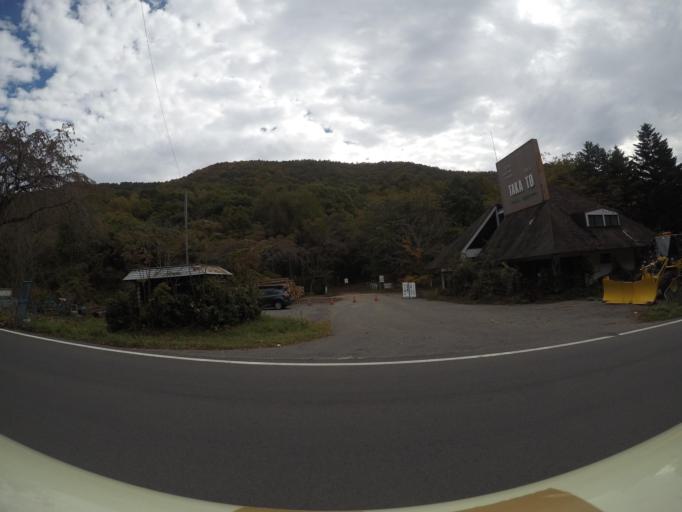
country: JP
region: Nagano
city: Chino
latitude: 35.9618
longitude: 138.1151
